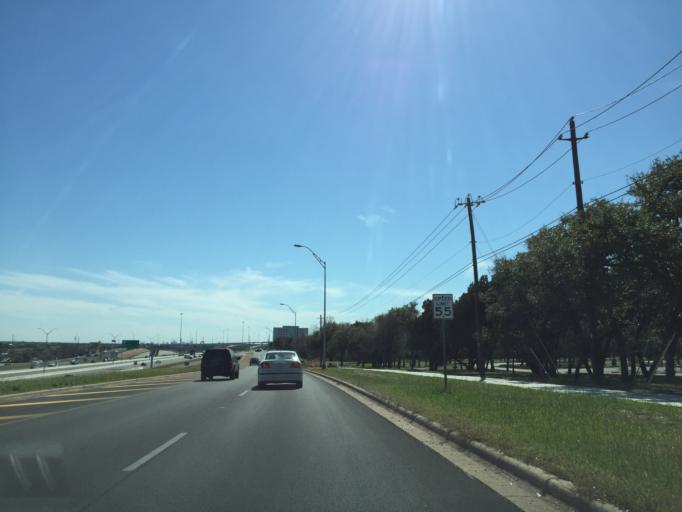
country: US
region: Texas
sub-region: Williamson County
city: Jollyville
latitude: 30.3952
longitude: -97.7337
